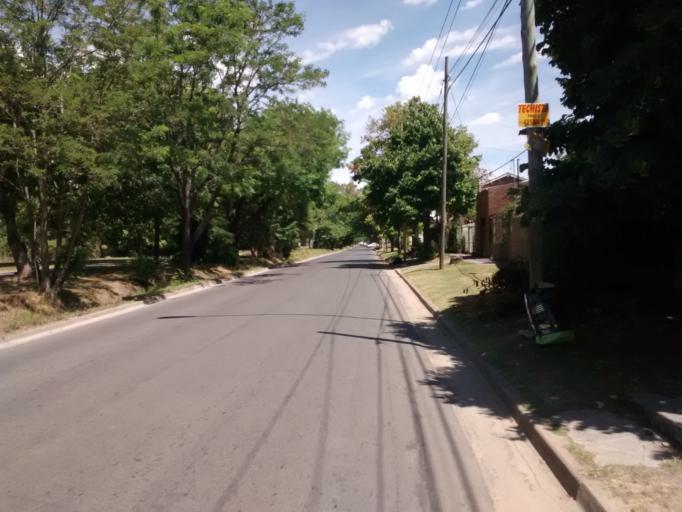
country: AR
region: Buenos Aires
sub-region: Partido de La Plata
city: La Plata
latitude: -34.8770
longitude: -58.0162
